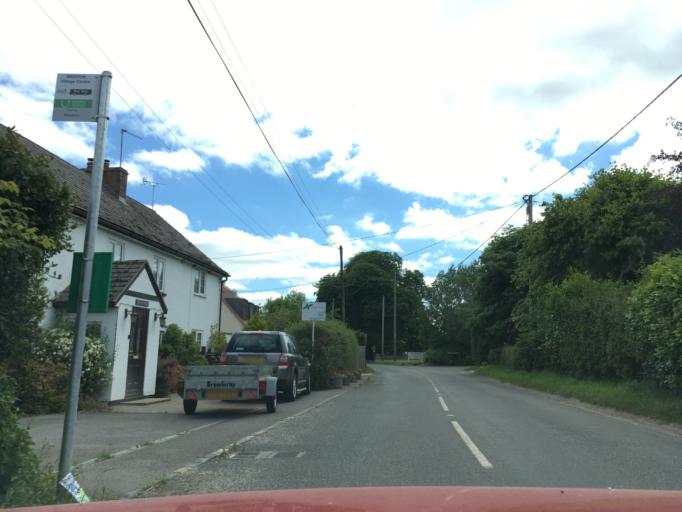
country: GB
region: England
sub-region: West Berkshire
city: Welford
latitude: 51.4610
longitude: -1.4268
